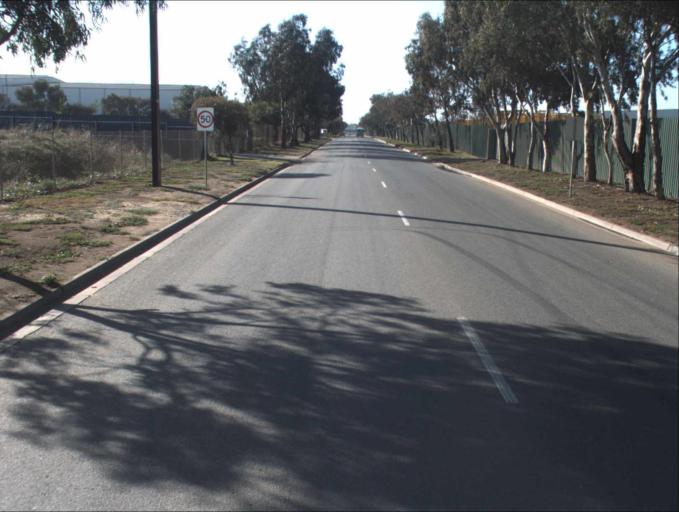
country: AU
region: South Australia
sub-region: Port Adelaide Enfield
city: Alberton
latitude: -34.8377
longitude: 138.5397
